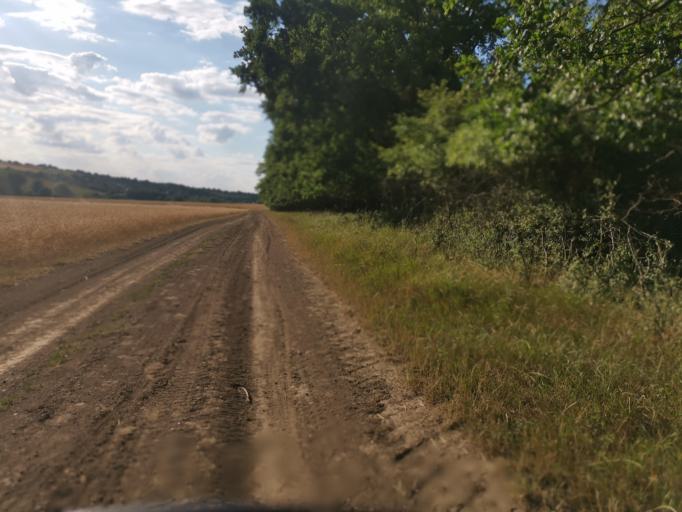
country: SK
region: Trnavsky
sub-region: Okres Skalica
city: Skalica
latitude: 48.8220
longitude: 17.2616
